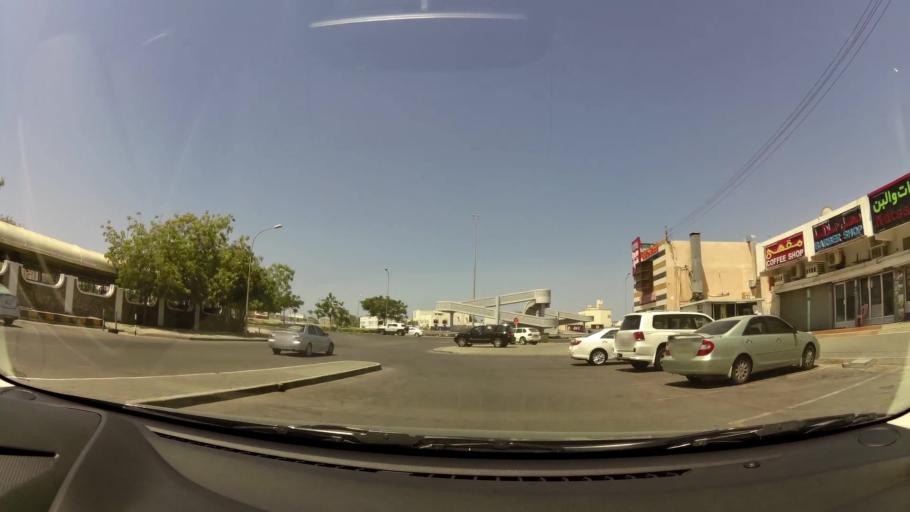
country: OM
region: Muhafazat Masqat
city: As Sib al Jadidah
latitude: 23.6329
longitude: 58.2297
